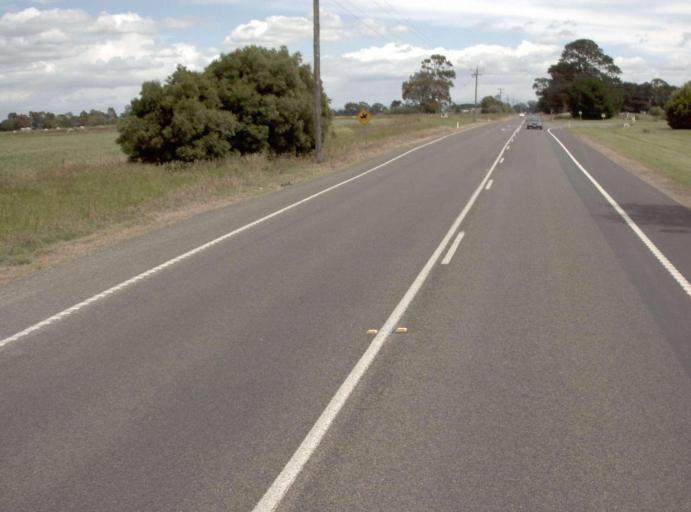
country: AU
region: Victoria
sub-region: Wellington
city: Sale
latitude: -38.0724
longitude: 147.0398
